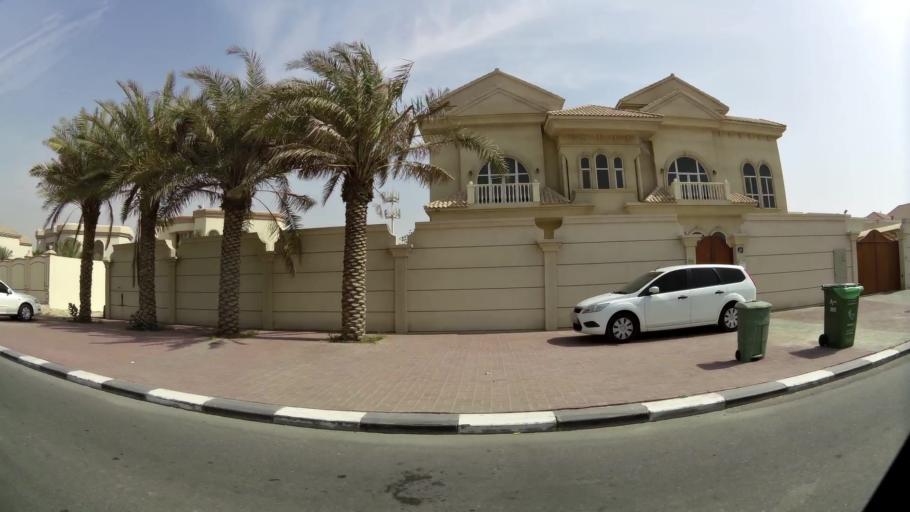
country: AE
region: Ash Shariqah
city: Sharjah
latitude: 25.2502
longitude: 55.4338
